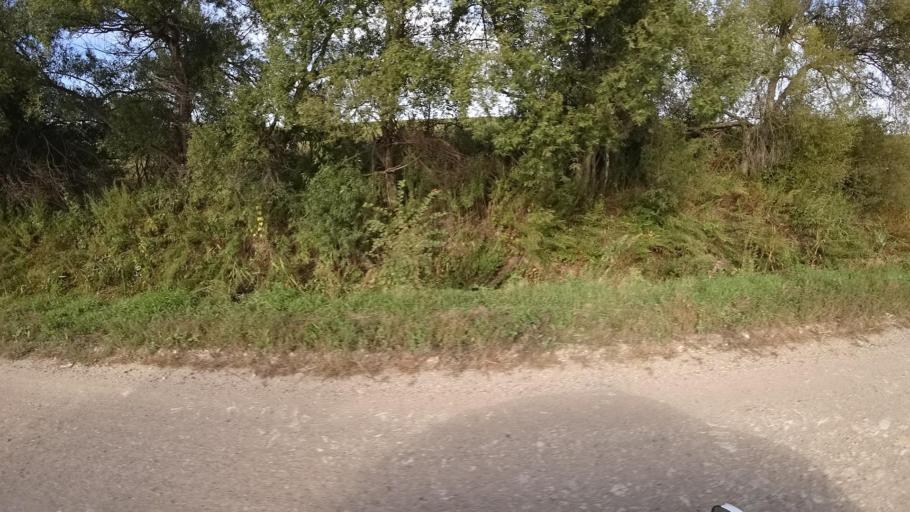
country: RU
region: Primorskiy
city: Dostoyevka
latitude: 44.3117
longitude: 133.4626
